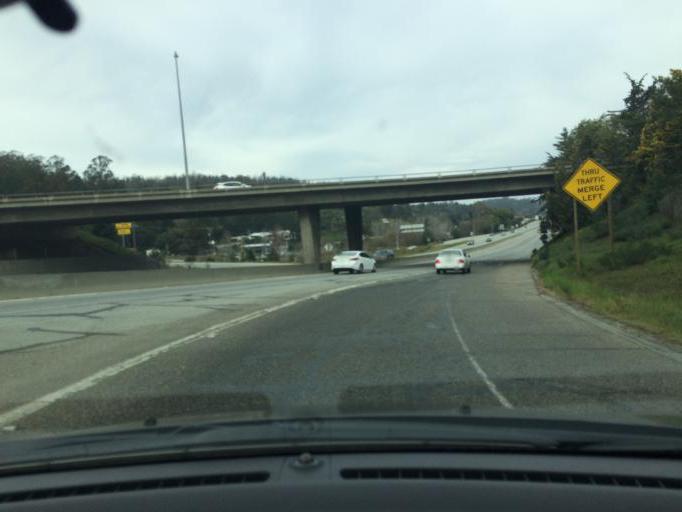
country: US
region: California
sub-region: Monterey County
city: Prunedale
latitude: 36.7891
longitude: -121.6675
